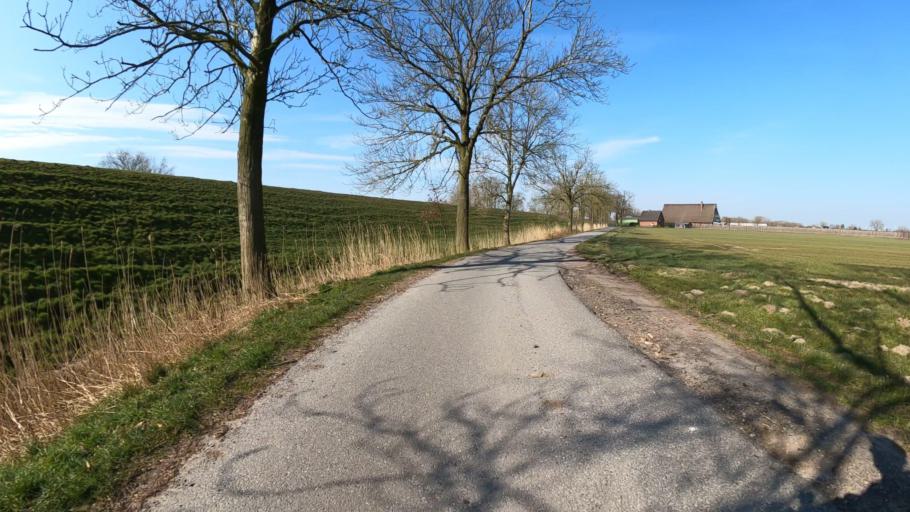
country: DE
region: Schleswig-Holstein
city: Seestermuhe
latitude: 53.6829
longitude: 9.5648
